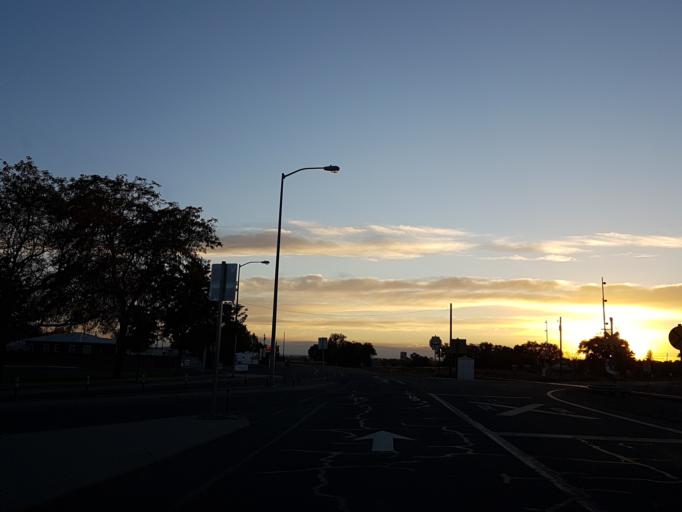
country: US
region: Oregon
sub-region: Malheur County
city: Vale
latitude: 43.9821
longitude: -117.2508
